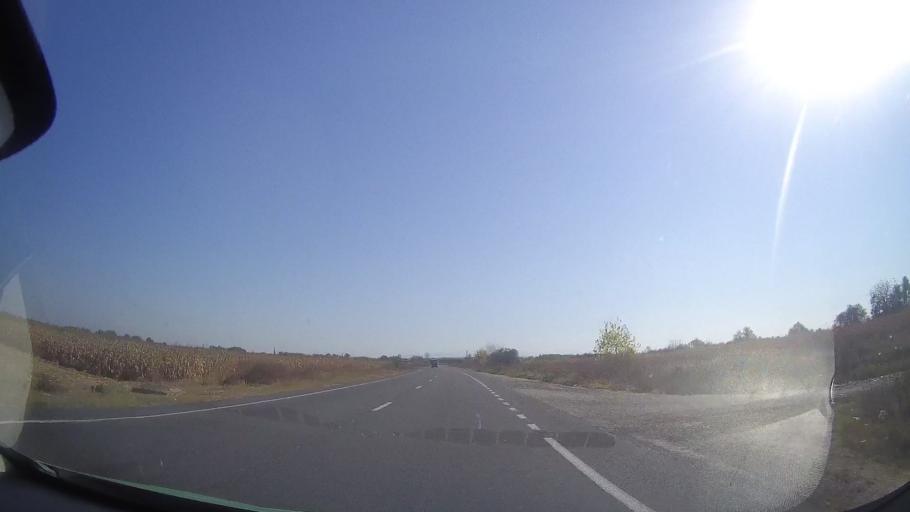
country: RO
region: Timis
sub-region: Comuna Costeiu
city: Costeiu
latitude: 45.7412
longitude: 21.8340
